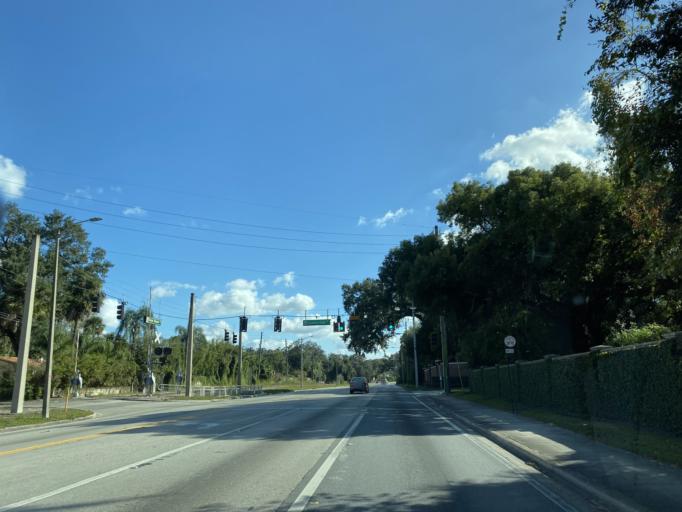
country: US
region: Florida
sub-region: Orange County
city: Orlando
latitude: 28.5603
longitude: -81.3976
